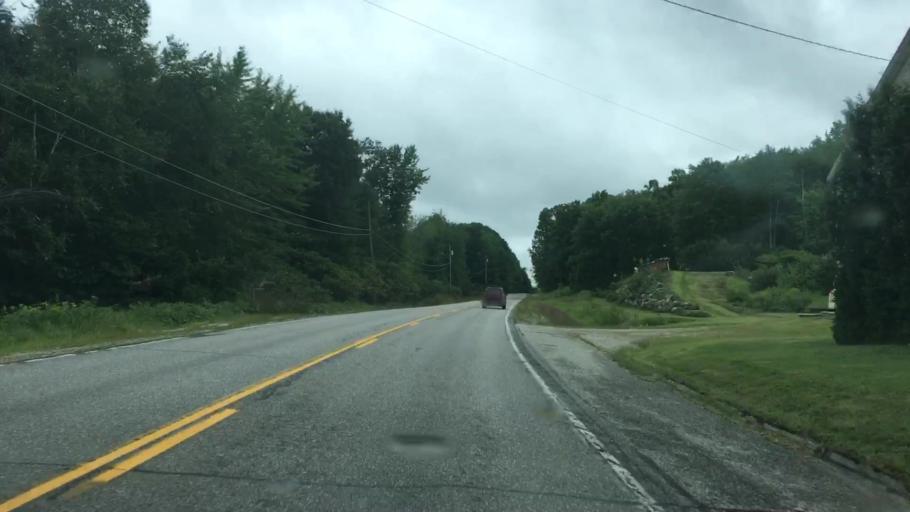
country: US
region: Maine
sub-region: Oxford County
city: Brownfield
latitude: 43.9580
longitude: -70.8987
